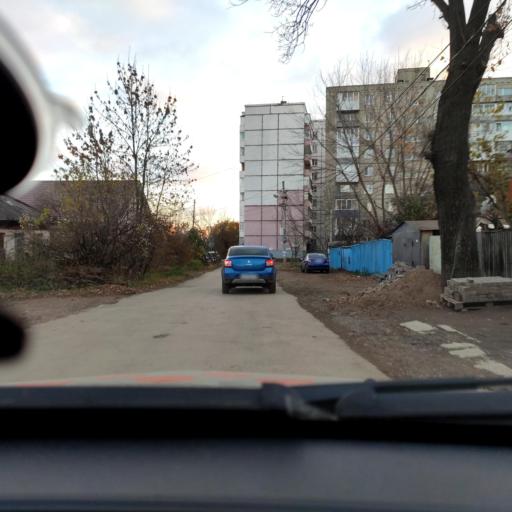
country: RU
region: Bashkortostan
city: Ufa
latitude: 54.7408
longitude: 56.0012
